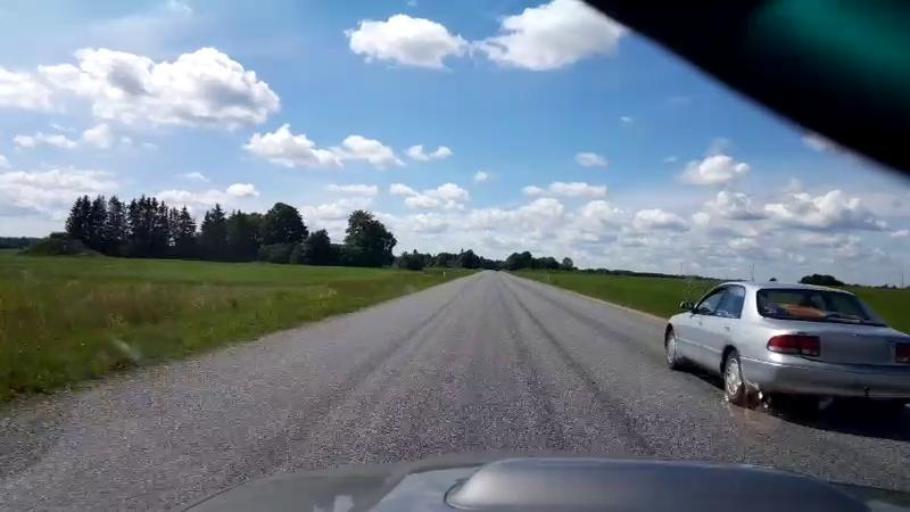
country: EE
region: Laeaene-Virumaa
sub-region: Tapa vald
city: Tapa
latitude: 59.2182
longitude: 25.8846
